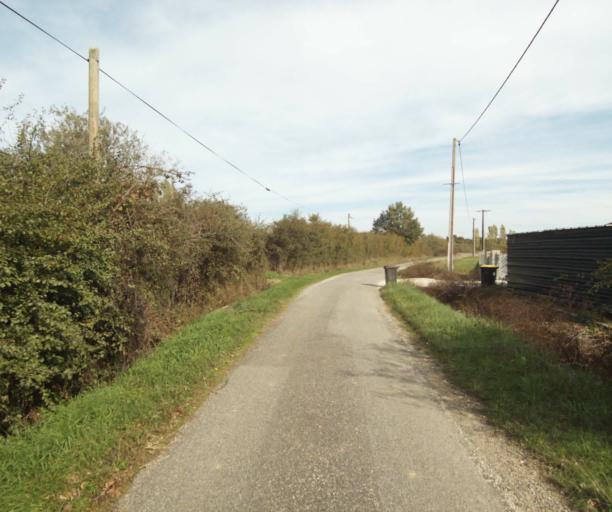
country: FR
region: Midi-Pyrenees
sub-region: Departement du Tarn-et-Garonne
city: Orgueil
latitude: 43.8945
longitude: 1.4017
